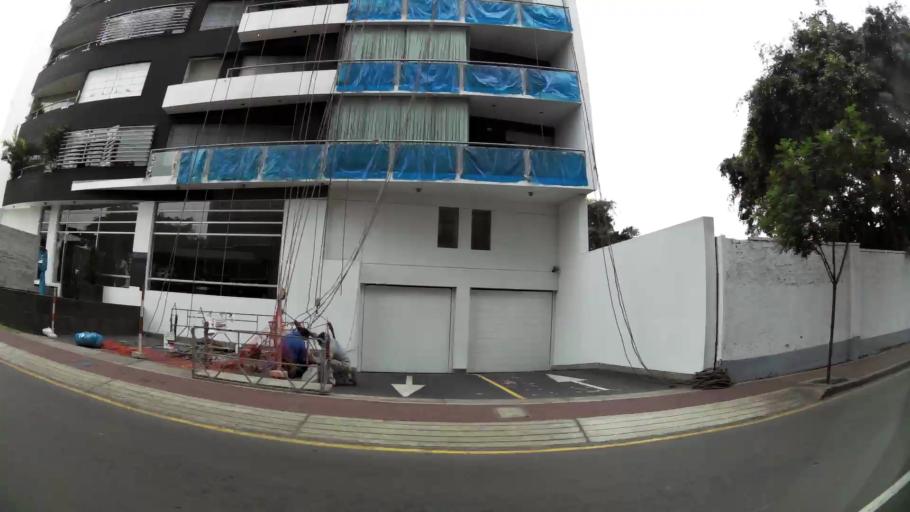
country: PE
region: Lima
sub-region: Lima
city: San Isidro
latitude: -12.1002
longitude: -77.0379
